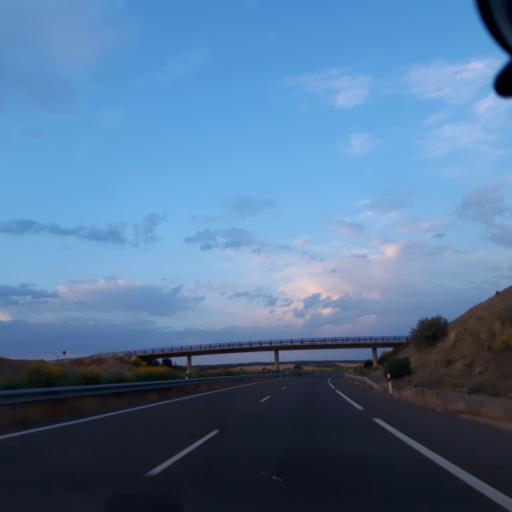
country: ES
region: Castille and Leon
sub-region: Provincia de Salamanca
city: Mozarbez
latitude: 40.8569
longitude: -5.6414
